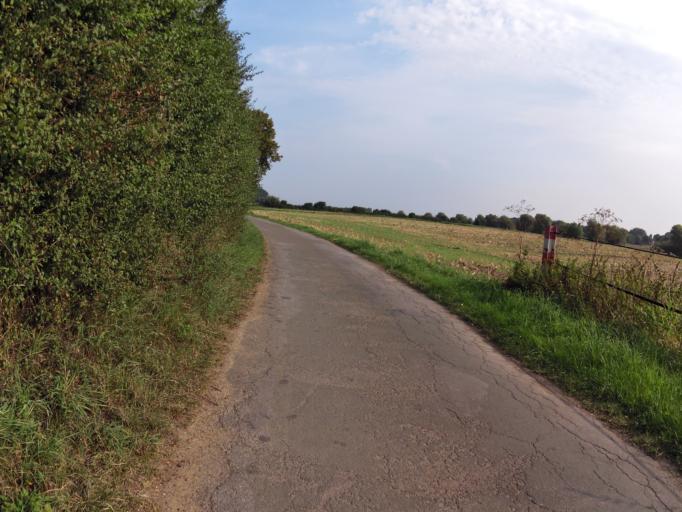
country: DE
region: Lower Saxony
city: Raddestorf
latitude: 52.4583
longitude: 9.0171
